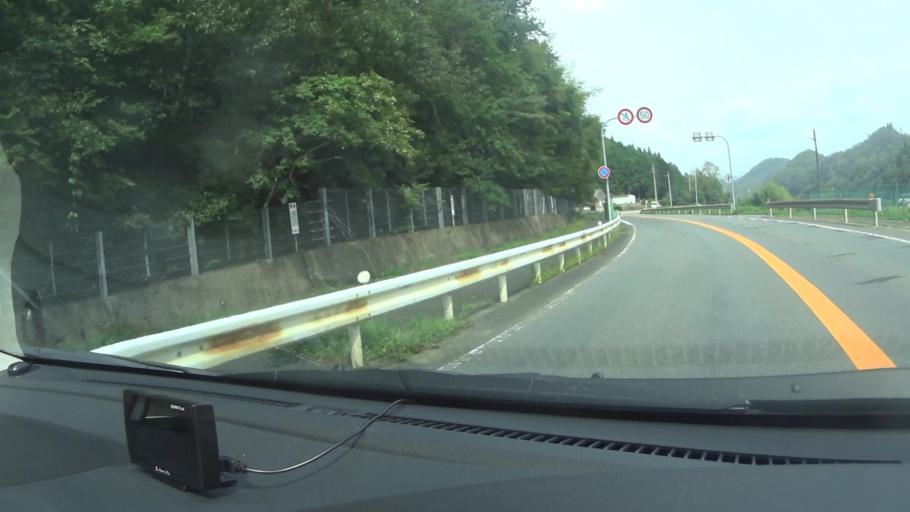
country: JP
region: Hyogo
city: Sasayama
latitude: 35.1520
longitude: 135.3554
